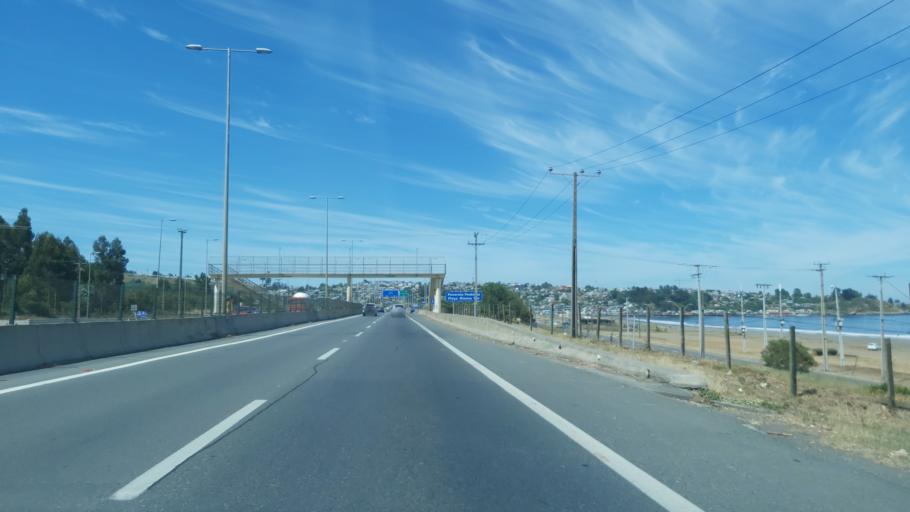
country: CL
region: Biobio
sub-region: Provincia de Concepcion
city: Lota
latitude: -37.0658
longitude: -73.1430
